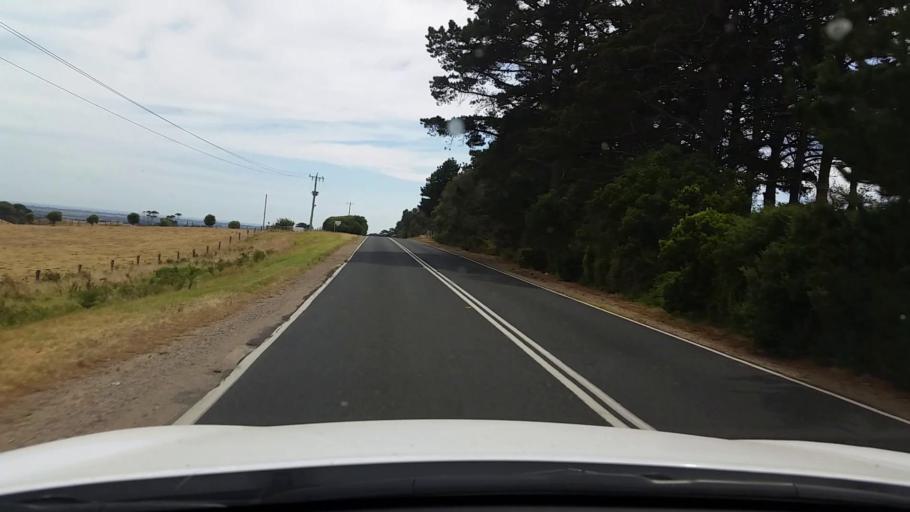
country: AU
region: Victoria
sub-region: Mornington Peninsula
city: Saint Andrews Beach
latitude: -38.4467
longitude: 144.8966
